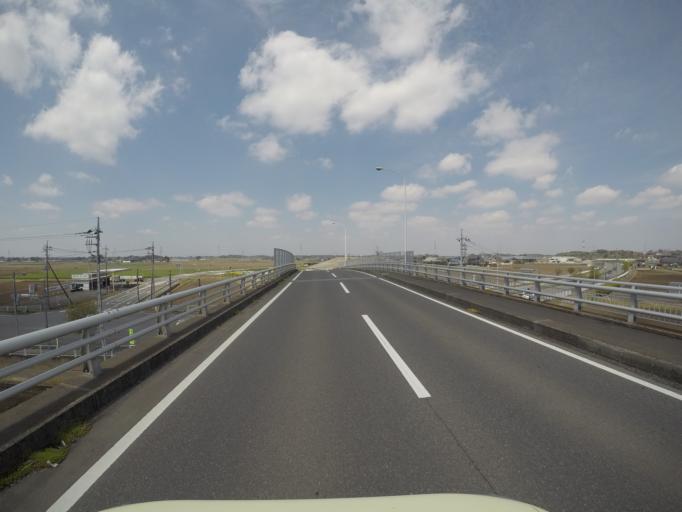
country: JP
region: Ibaraki
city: Shimodate
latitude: 36.3360
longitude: 139.9720
